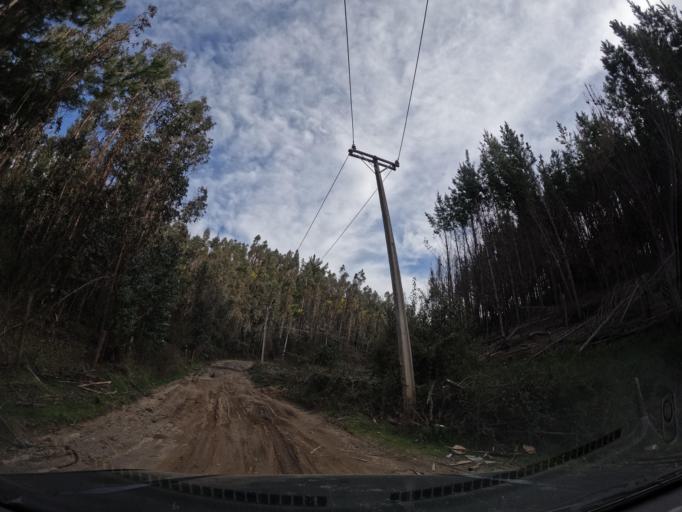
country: CL
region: Biobio
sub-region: Provincia de Concepcion
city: Chiguayante
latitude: -37.0169
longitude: -72.9120
